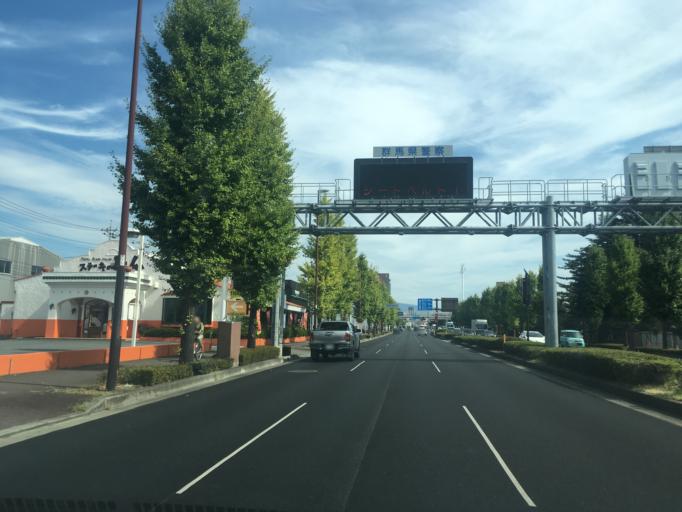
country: JP
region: Gunma
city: Maebashi-shi
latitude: 36.3816
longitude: 139.0407
